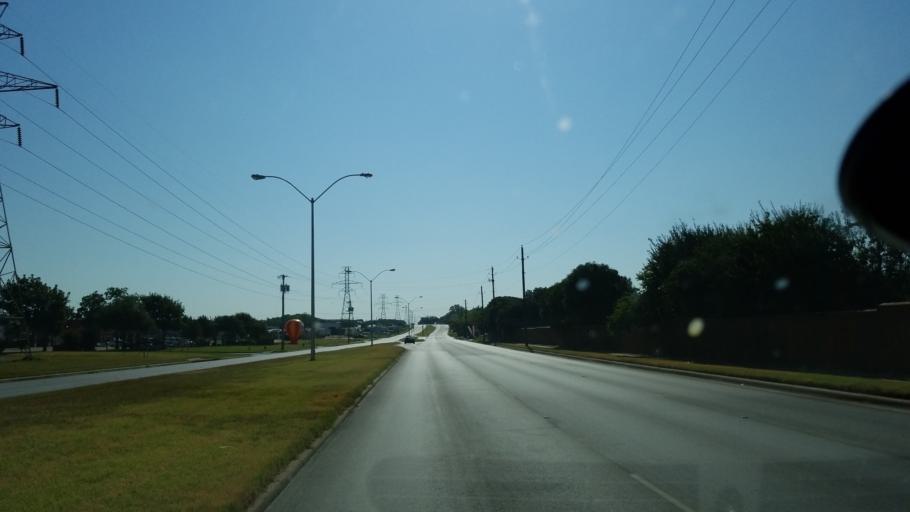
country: US
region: Texas
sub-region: Tarrant County
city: Euless
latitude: 32.8197
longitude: -97.0855
